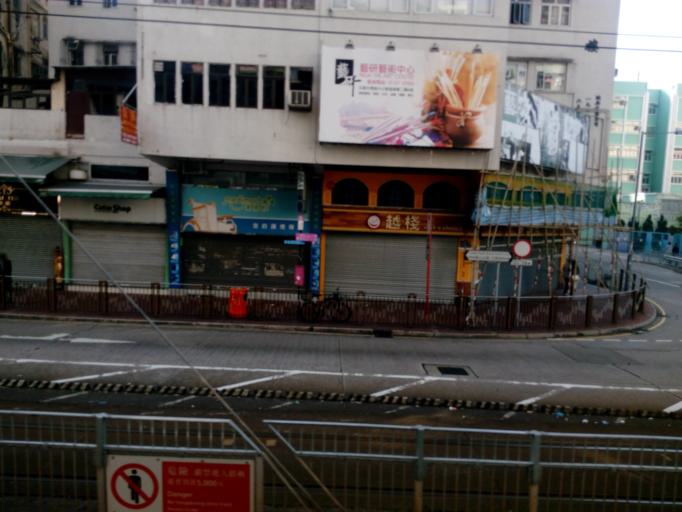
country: HK
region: Yuen Long
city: Yuen Long Kau Hui
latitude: 22.4445
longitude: 114.0246
